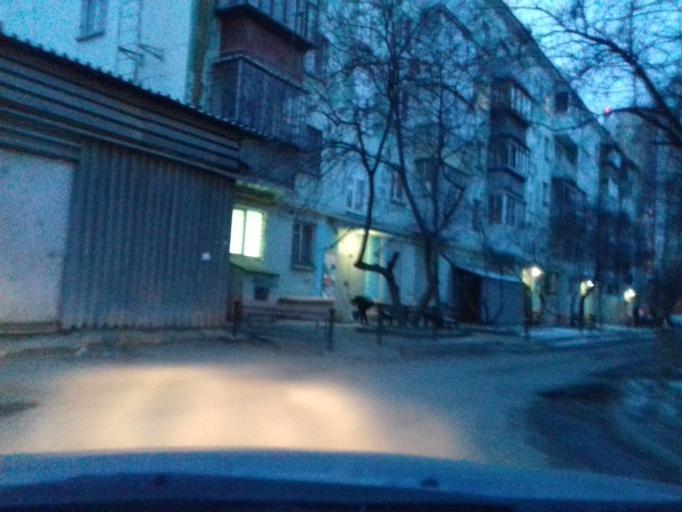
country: RU
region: Sverdlovsk
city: Istok
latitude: 56.7506
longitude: 60.6948
